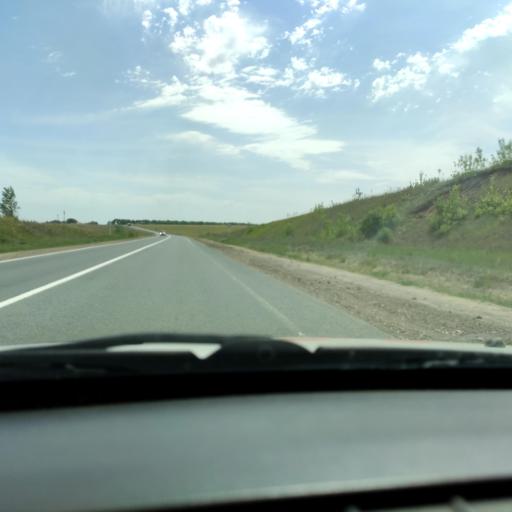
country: RU
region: Samara
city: Mirnyy
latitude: 53.5957
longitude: 50.2776
